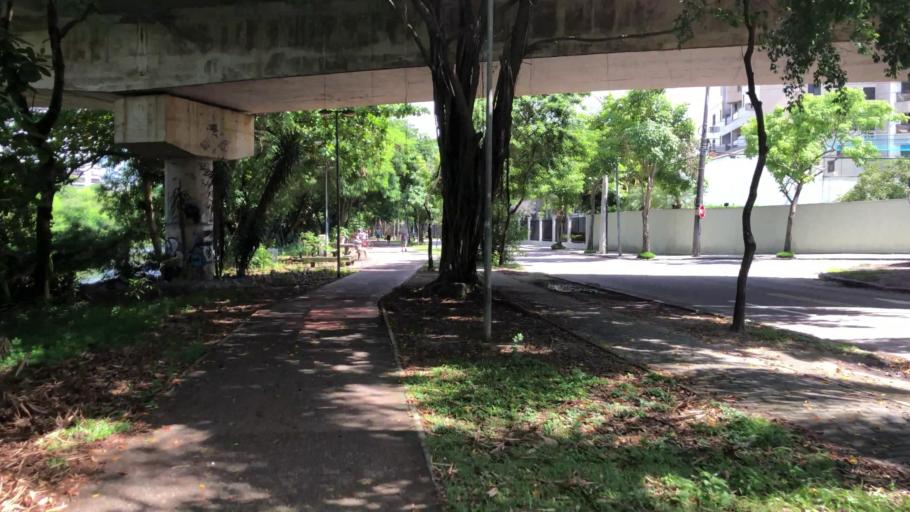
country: BR
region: Rio de Janeiro
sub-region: Rio De Janeiro
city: Rio de Janeiro
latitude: -23.0073
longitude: -43.3191
